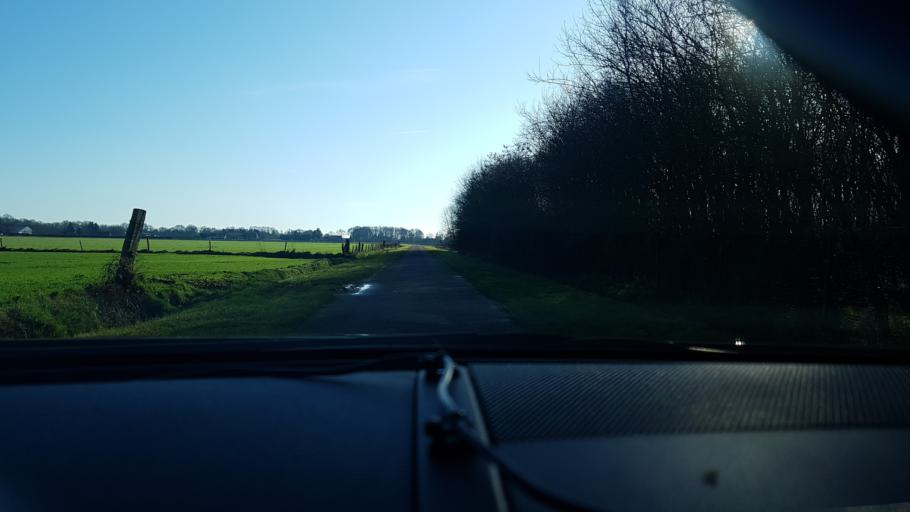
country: NL
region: Limburg
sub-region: Gemeente Leudal
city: Haelen
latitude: 51.2791
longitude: 5.9849
